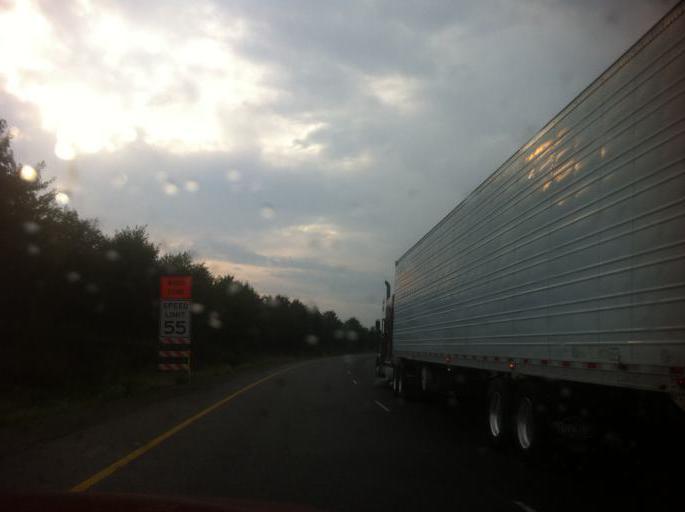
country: US
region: Pennsylvania
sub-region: Clarion County
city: Knox
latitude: 41.1968
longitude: -79.4800
